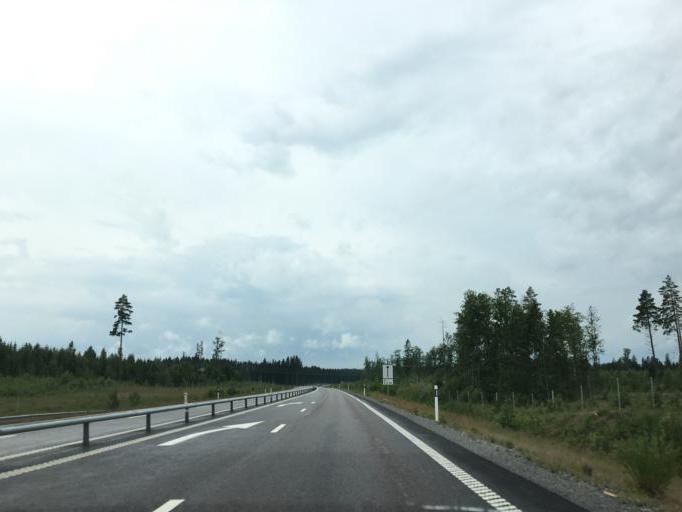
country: SE
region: Soedermanland
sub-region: Katrineholms Kommun
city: Katrineholm
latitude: 58.9505
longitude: 16.2185
